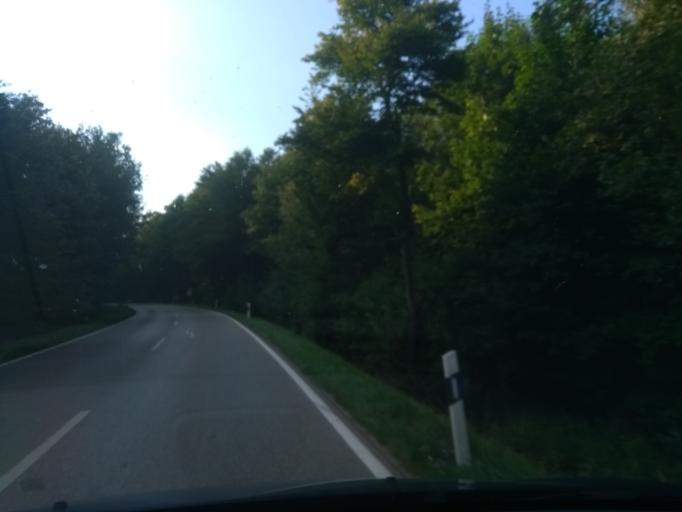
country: DE
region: Bavaria
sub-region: Upper Bavaria
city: Schwabhausen
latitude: 48.3083
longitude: 11.3886
